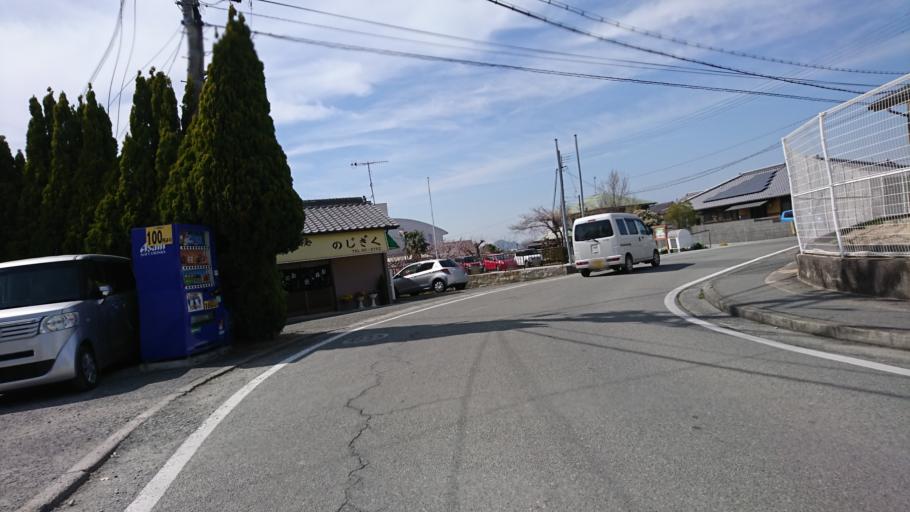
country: JP
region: Hyogo
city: Kakogawacho-honmachi
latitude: 34.7489
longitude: 134.9023
